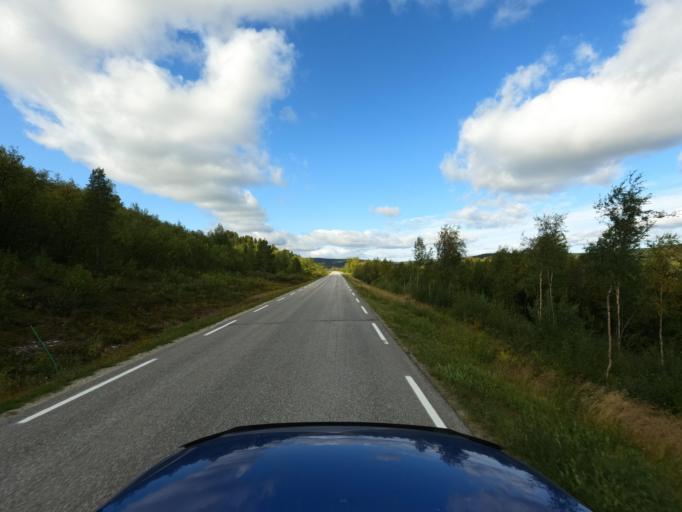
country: NO
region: Finnmark Fylke
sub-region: Karasjok
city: Karasjohka
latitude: 69.4522
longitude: 25.5791
